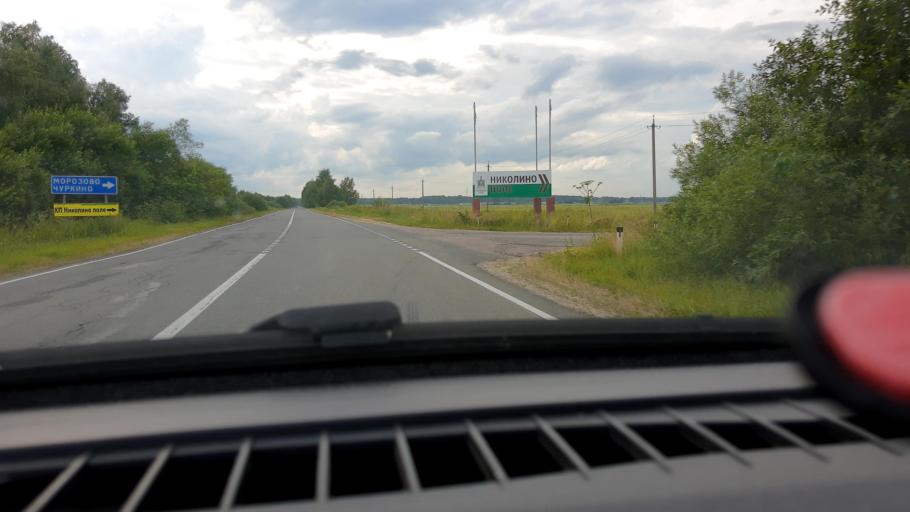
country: RU
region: Nizjnij Novgorod
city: Neklyudovo
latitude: 56.5241
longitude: 43.8672
